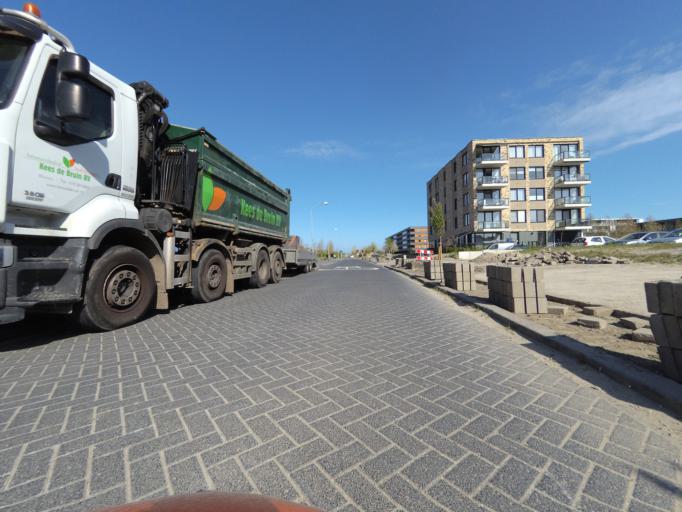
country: NL
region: Flevoland
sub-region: Gemeente Almere
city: Almere Stad
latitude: 52.3923
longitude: 5.1749
